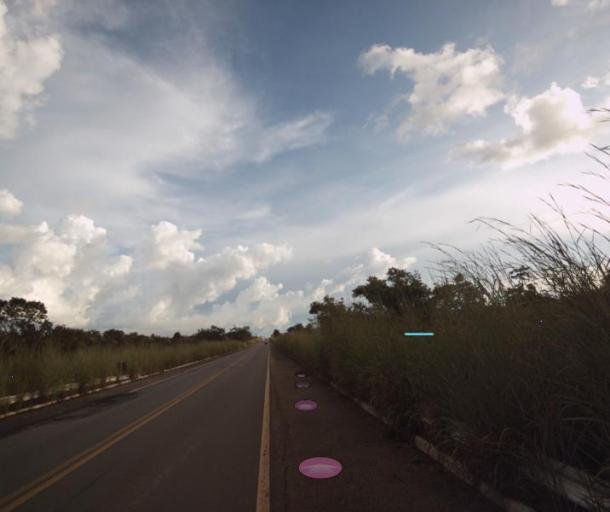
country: BR
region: Goias
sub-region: Niquelandia
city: Niquelandia
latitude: -14.7336
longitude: -48.6138
